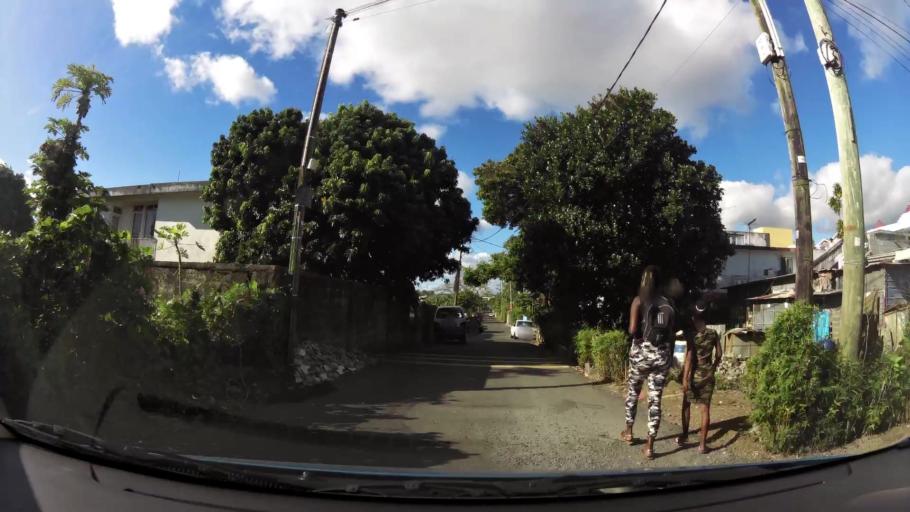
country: MU
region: Plaines Wilhems
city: Vacoas
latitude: -20.2893
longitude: 57.4923
